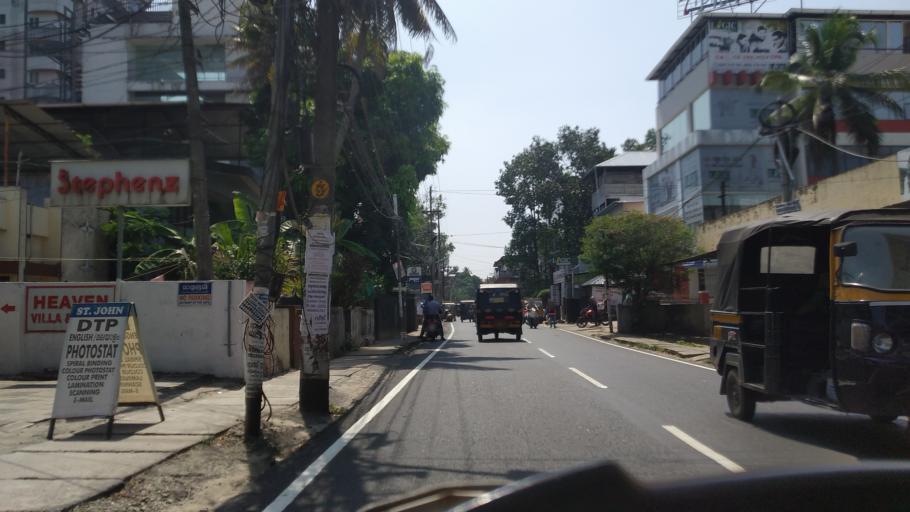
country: IN
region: Kerala
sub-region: Ernakulam
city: Elur
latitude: 9.9990
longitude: 76.3074
